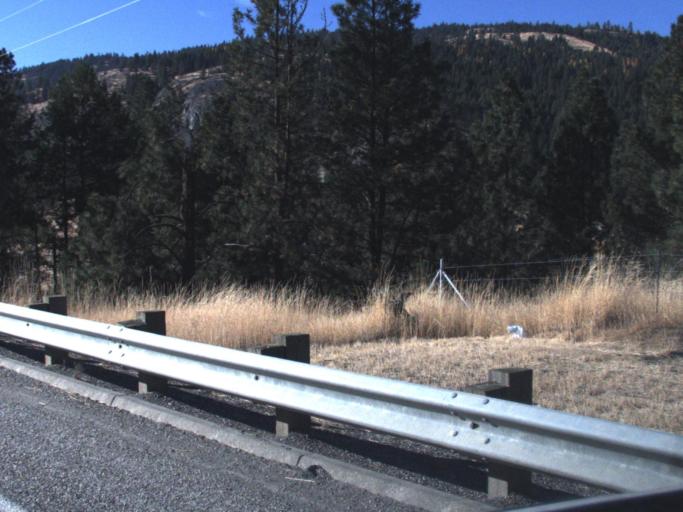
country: US
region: Washington
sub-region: Ferry County
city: Republic
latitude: 48.6919
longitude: -118.6605
